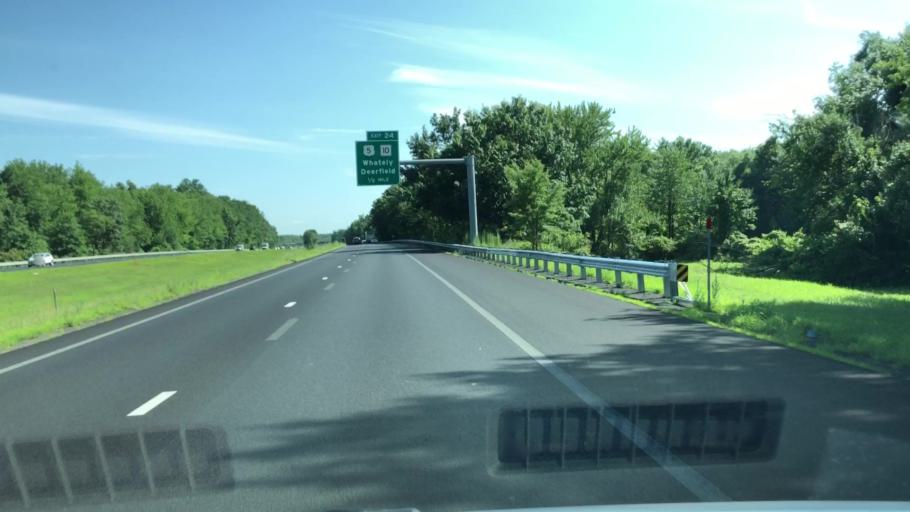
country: US
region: Massachusetts
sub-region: Franklin County
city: South Deerfield
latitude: 42.4763
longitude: -72.6173
